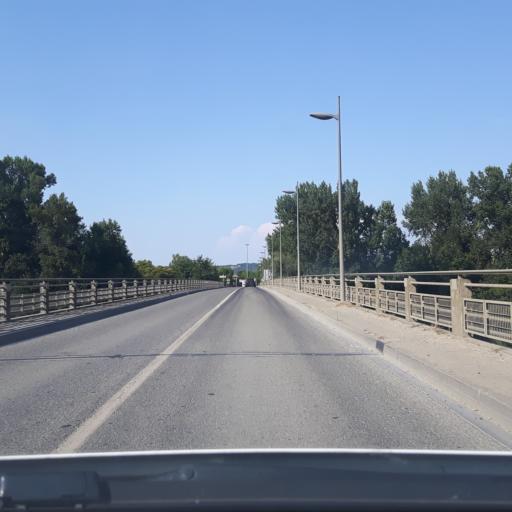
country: FR
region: Midi-Pyrenees
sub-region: Departement de la Haute-Garonne
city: Ondes
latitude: 43.7774
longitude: 1.3066
